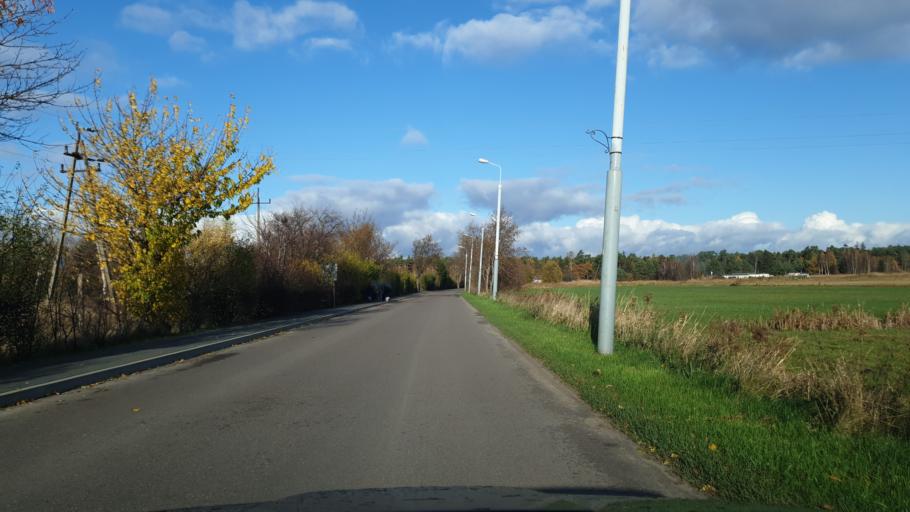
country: PL
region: Pomeranian Voivodeship
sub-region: Powiat pucki
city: Jastrzebia Gora
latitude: 54.8262
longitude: 18.2439
